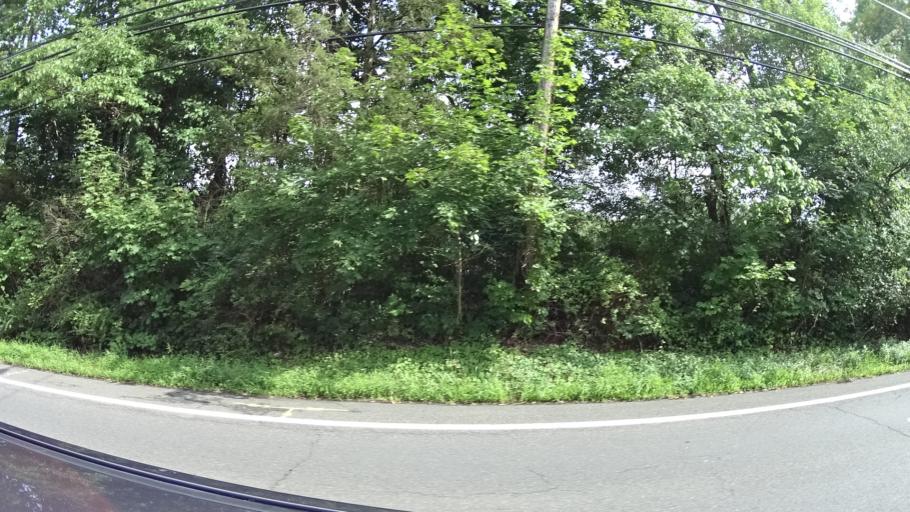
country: US
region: New Jersey
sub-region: Union County
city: Berkeley Heights
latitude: 40.6711
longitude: -74.4755
